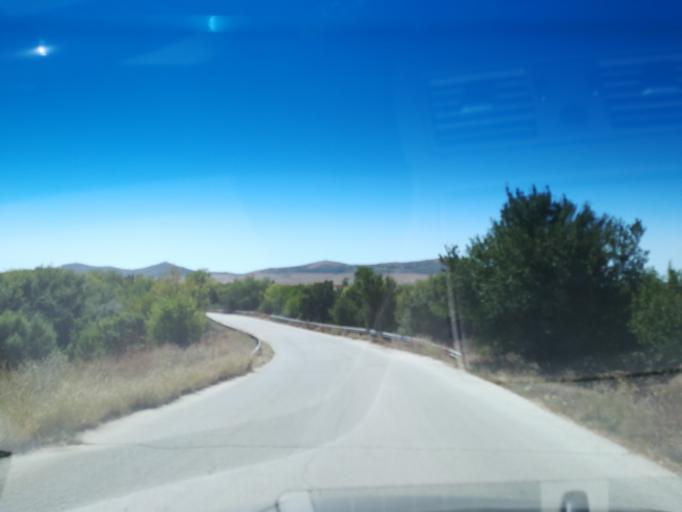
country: BG
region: Pazardzhik
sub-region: Obshtina Strelcha
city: Strelcha
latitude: 42.3583
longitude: 24.3995
